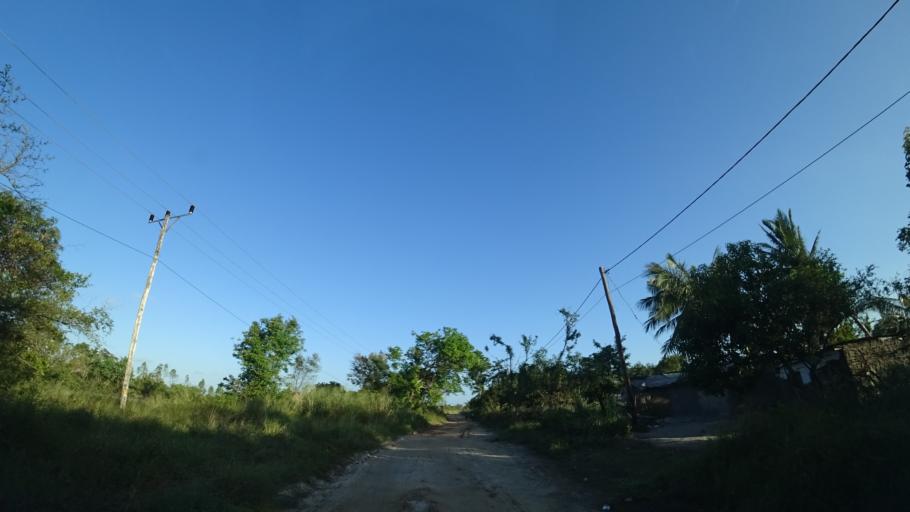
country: MZ
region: Sofala
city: Dondo
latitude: -19.3888
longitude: 34.7083
